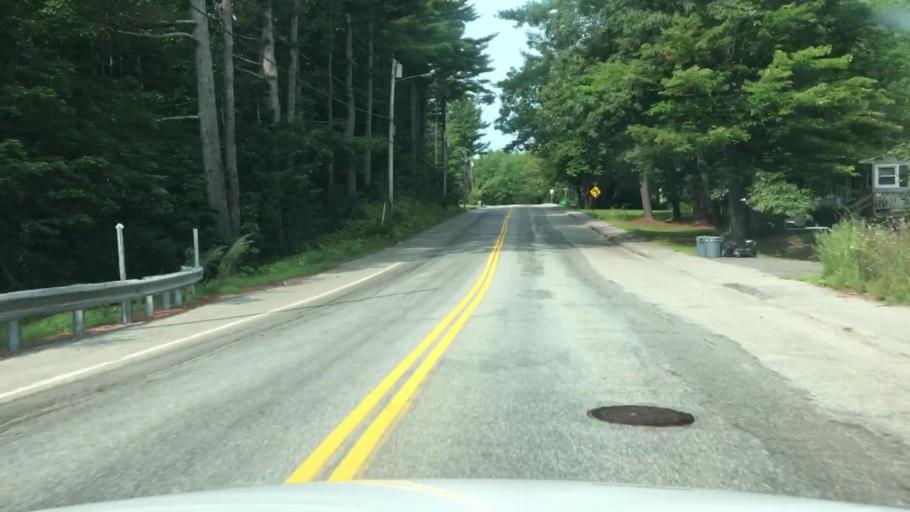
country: US
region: Maine
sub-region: Kennebec County
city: Augusta
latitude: 44.3199
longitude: -69.7521
